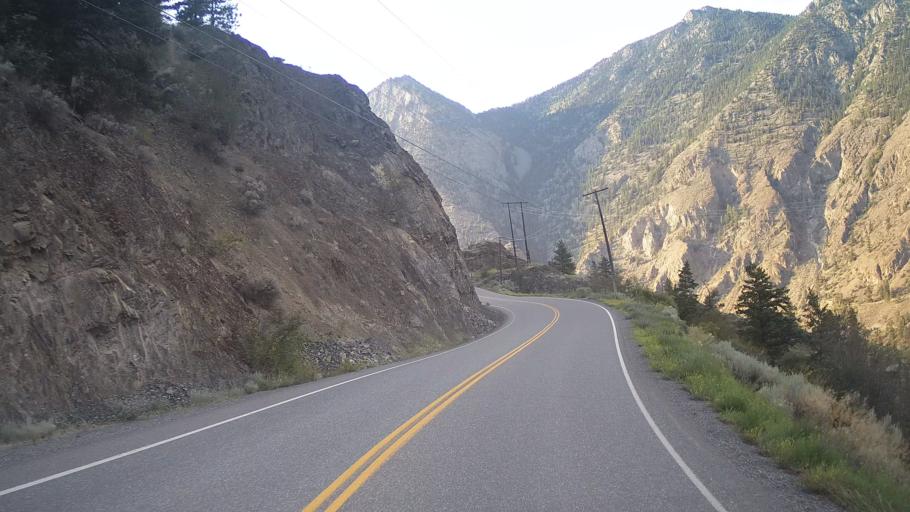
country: CA
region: British Columbia
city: Lillooet
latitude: 50.7508
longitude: -121.8930
